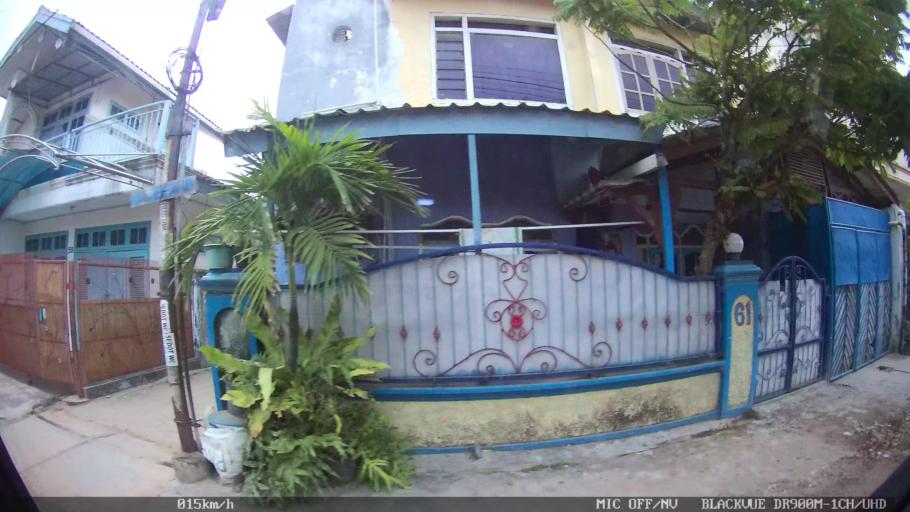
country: ID
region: Lampung
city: Bandarlampung
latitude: -5.4218
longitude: 105.2783
